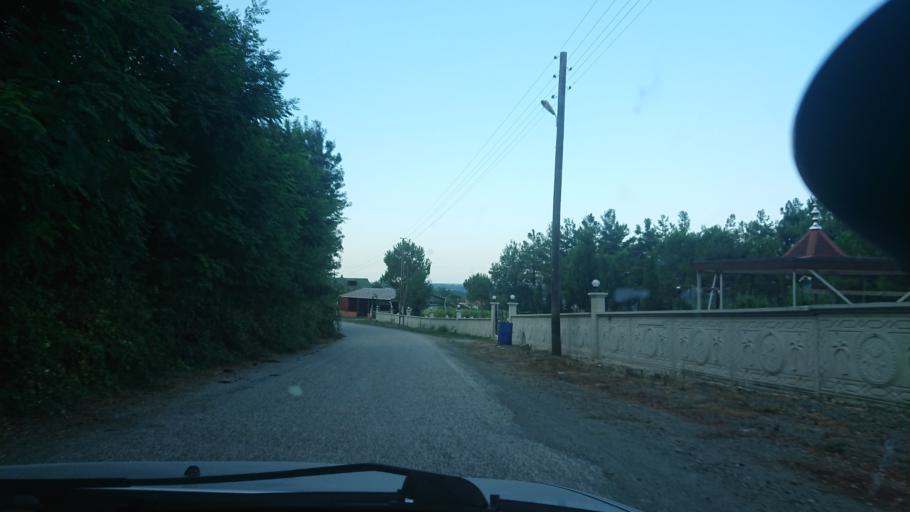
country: TR
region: Samsun
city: Dikbiyik
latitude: 41.1739
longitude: 36.5417
